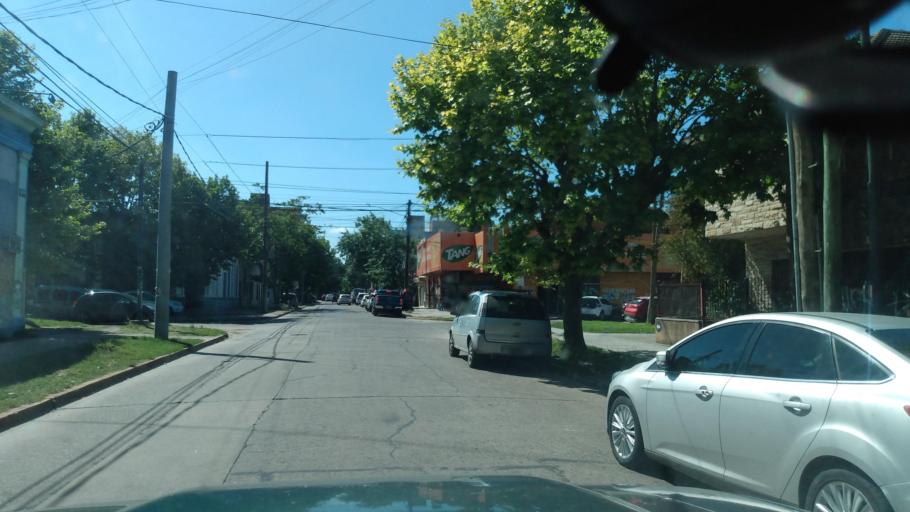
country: AR
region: Buenos Aires
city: Hurlingham
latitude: -34.5408
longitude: -58.7082
